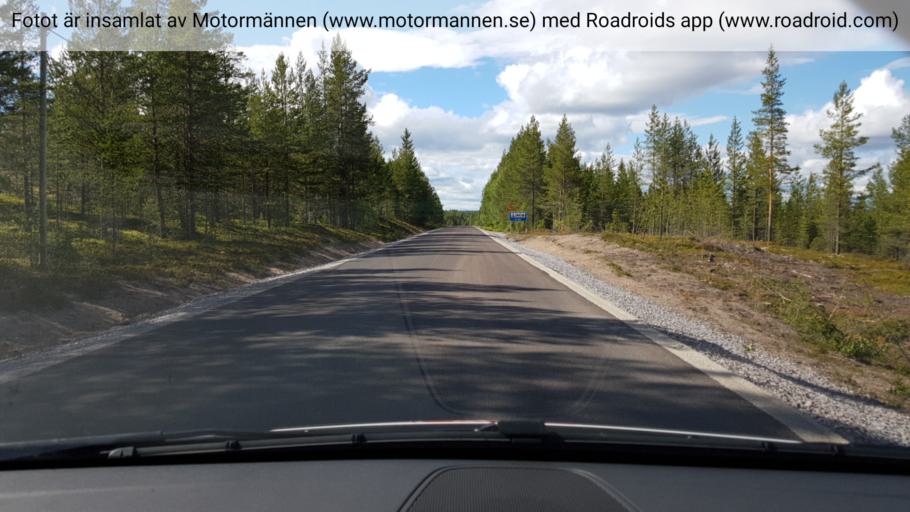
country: SE
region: Jaemtland
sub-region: Harjedalens Kommun
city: Sveg
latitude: 61.8313
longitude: 14.0891
